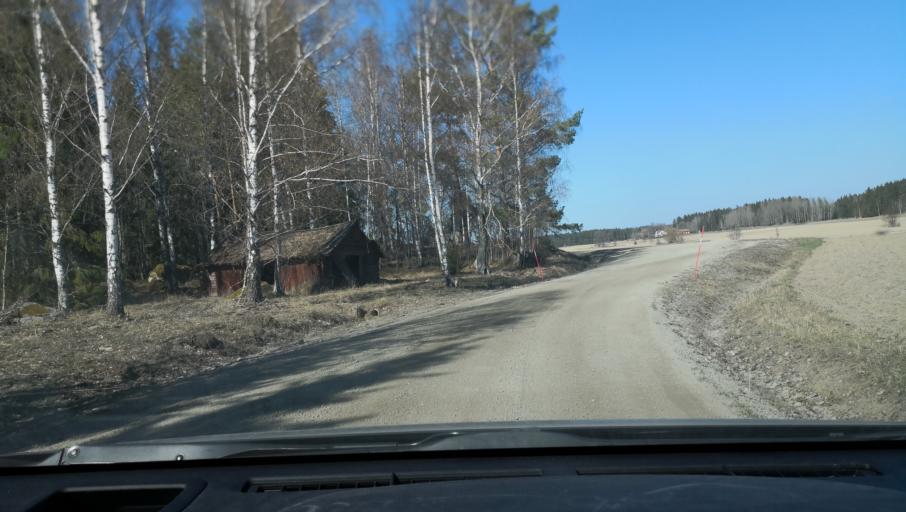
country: SE
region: Vaestmanland
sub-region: Sala Kommun
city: Sala
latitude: 59.8851
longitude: 16.5274
